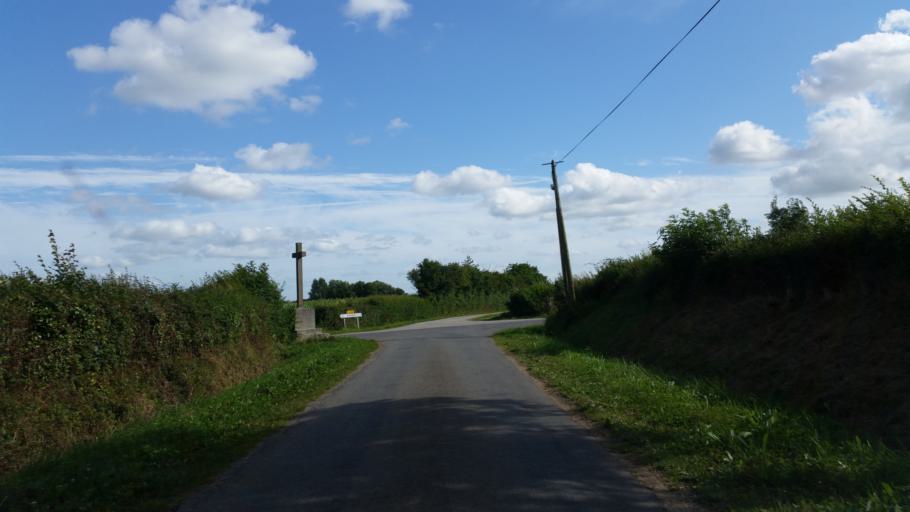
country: FR
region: Lower Normandy
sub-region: Departement de la Manche
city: Sainte-Mere-Eglise
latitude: 49.4524
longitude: -1.2915
